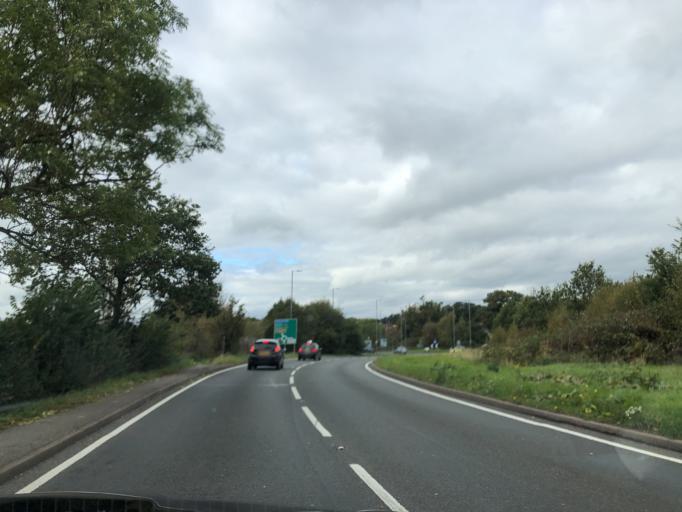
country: GB
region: England
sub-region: Warwickshire
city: Royal Leamington Spa
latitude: 52.3236
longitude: -1.5520
